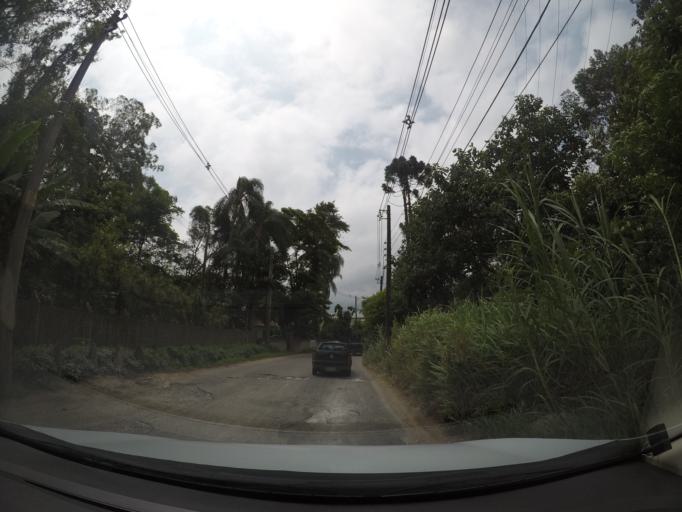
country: BR
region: Sao Paulo
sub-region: Itaquaquecetuba
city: Itaquaquecetuba
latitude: -23.4460
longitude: -46.3922
